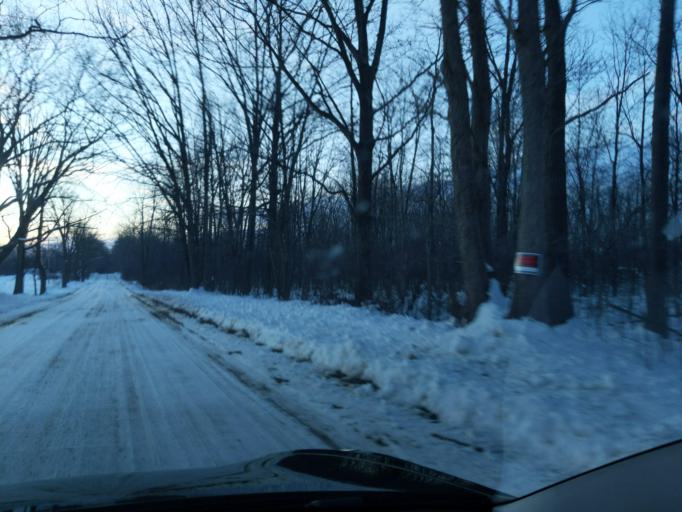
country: US
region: Michigan
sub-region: Ingham County
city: Williamston
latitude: 42.5704
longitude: -84.3195
